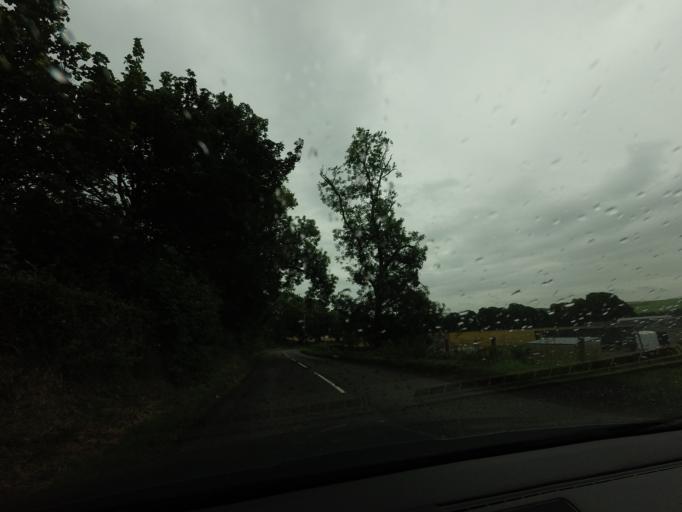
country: GB
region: Scotland
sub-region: Aberdeenshire
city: Turriff
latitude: 57.5402
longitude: -2.5067
